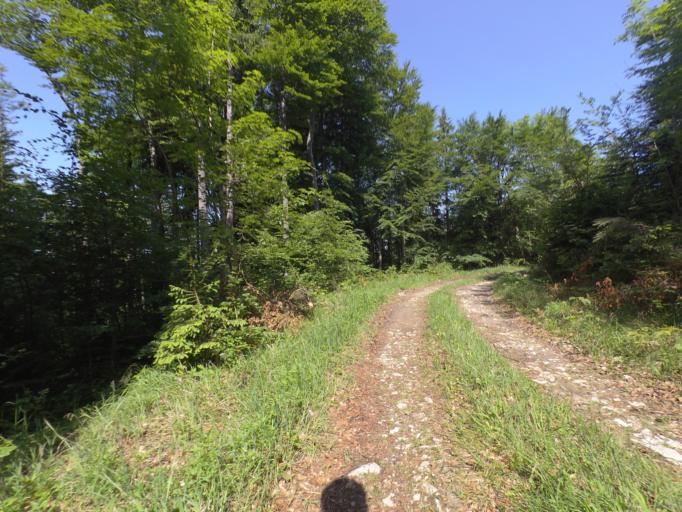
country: AT
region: Salzburg
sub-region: Politischer Bezirk Salzburg-Umgebung
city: Koppl
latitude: 47.7800
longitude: 13.1319
